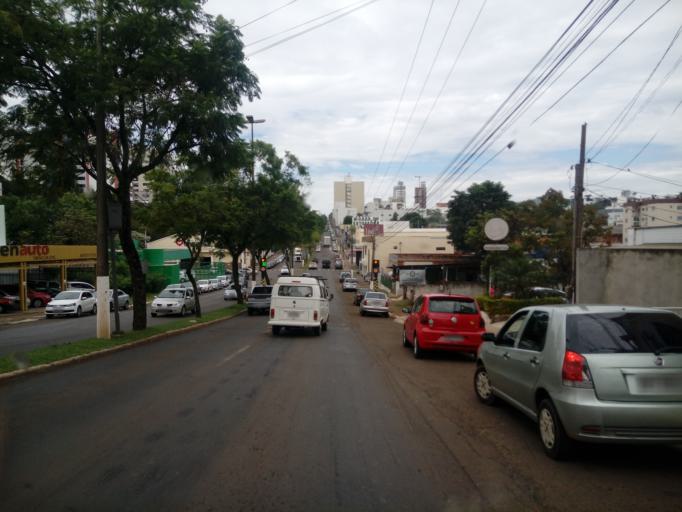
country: BR
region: Santa Catarina
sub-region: Chapeco
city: Chapeco
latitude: -27.0993
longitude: -52.6210
